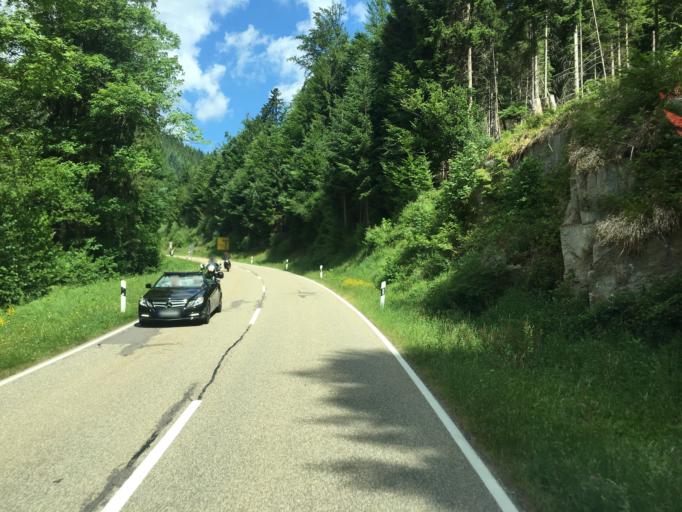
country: DE
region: Baden-Wuerttemberg
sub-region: Karlsruhe Region
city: Forbach
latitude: 48.6376
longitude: 8.3418
